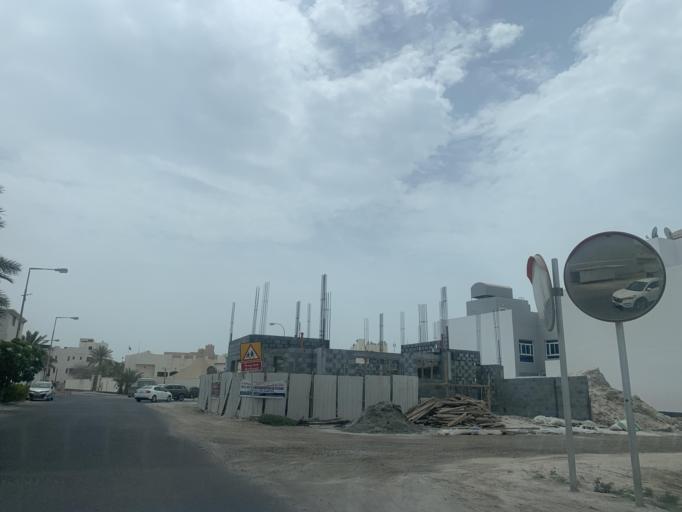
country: BH
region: Muharraq
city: Al Muharraq
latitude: 26.2817
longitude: 50.6318
